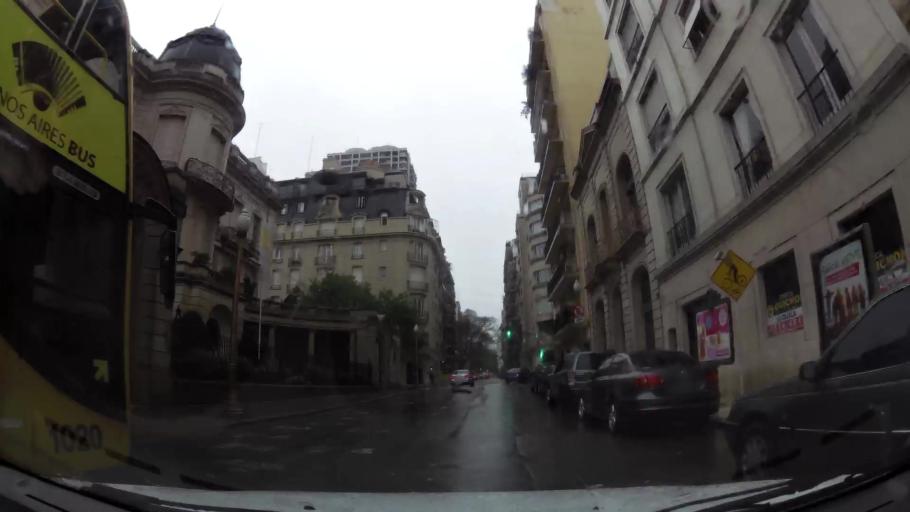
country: AR
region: Buenos Aires F.D.
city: Retiro
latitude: -34.5895
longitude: -58.3864
